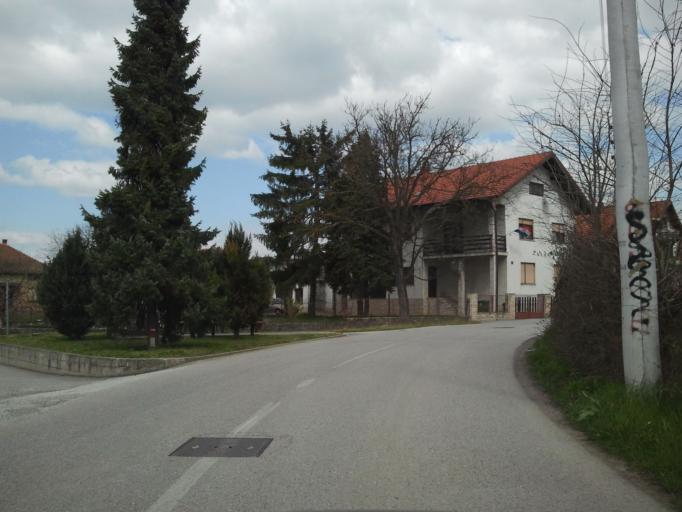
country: HR
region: Grad Zagreb
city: Zadvorsko
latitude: 45.7436
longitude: 15.9580
